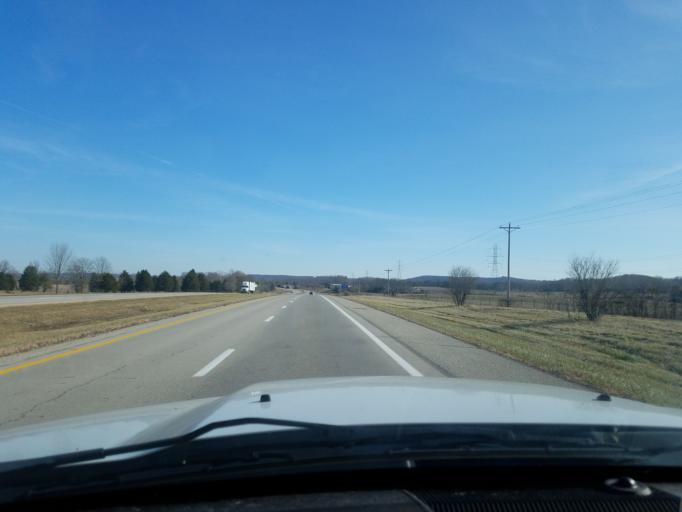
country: US
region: Ohio
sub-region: Adams County
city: Peebles
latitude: 38.9358
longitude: -83.4015
